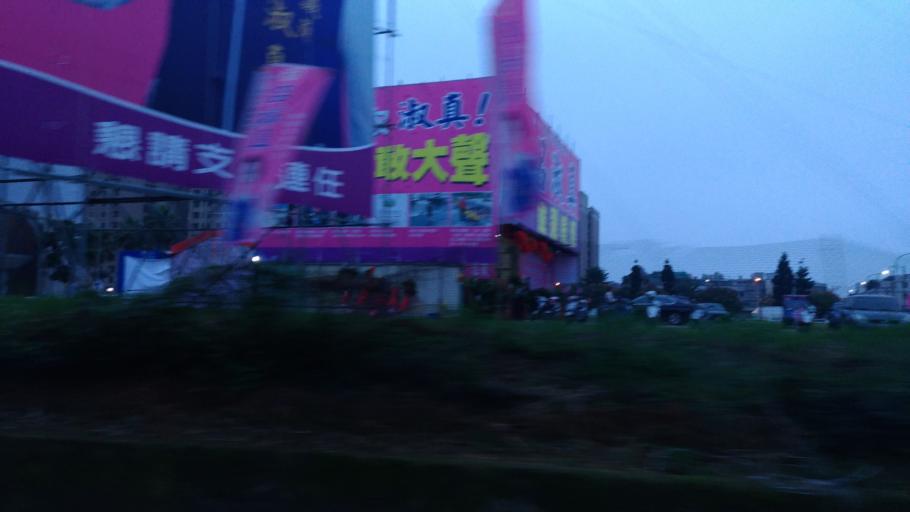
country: TW
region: Taiwan
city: Taoyuan City
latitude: 24.9559
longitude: 121.2944
